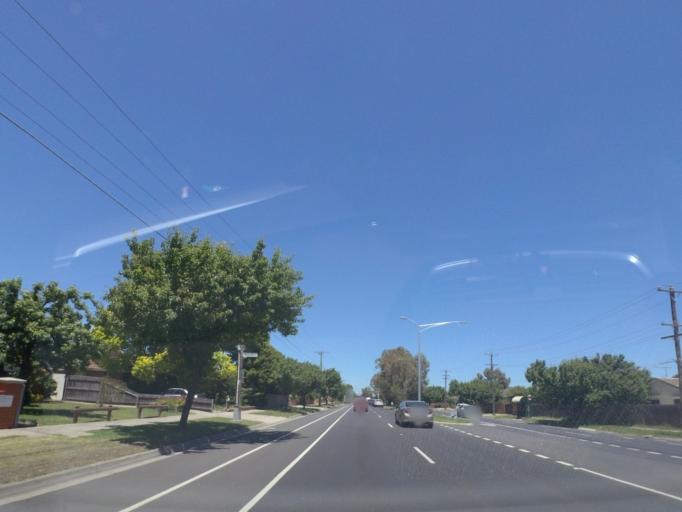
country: AU
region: Victoria
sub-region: Whittlesea
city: Thomastown
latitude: -37.6800
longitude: 145.0300
